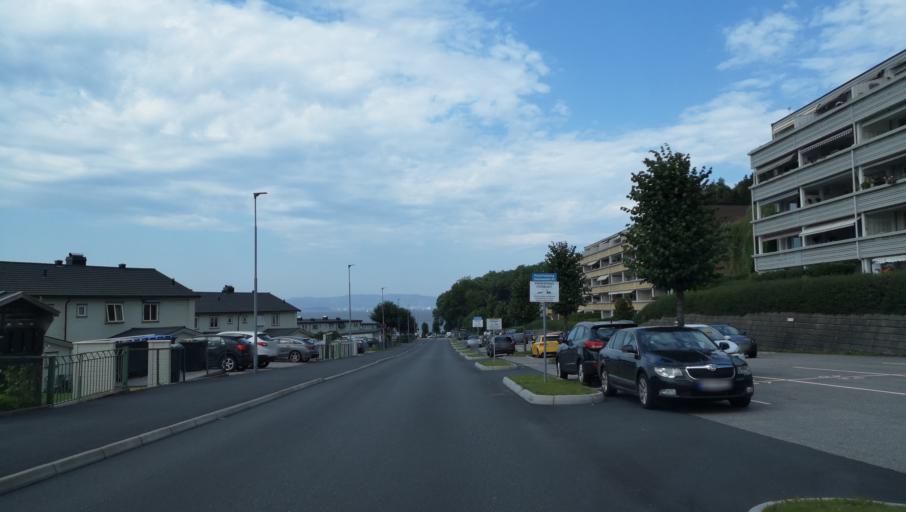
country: NO
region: Ostfold
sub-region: Moss
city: Moss
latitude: 59.4453
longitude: 10.6178
